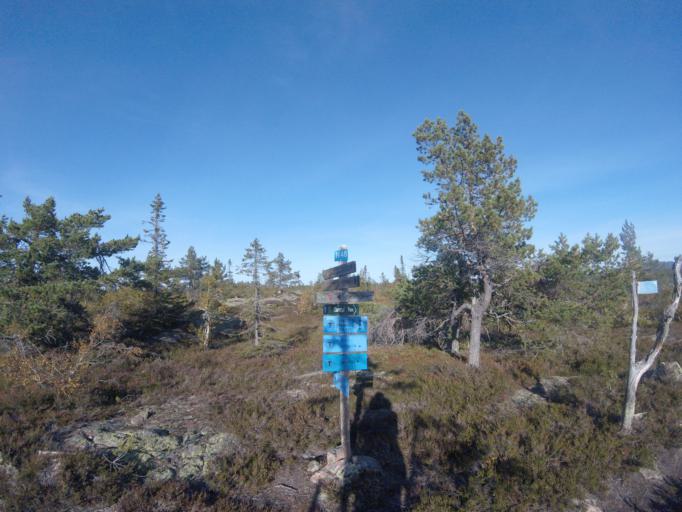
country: NO
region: Telemark
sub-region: Notodden
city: Notodden
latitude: 59.6867
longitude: 9.3688
